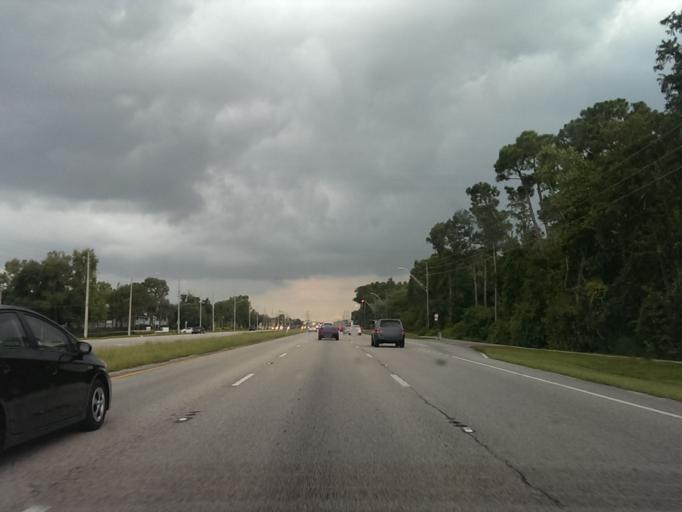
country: US
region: Florida
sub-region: Orange County
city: Orlovista
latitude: 28.5005
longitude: -81.4591
